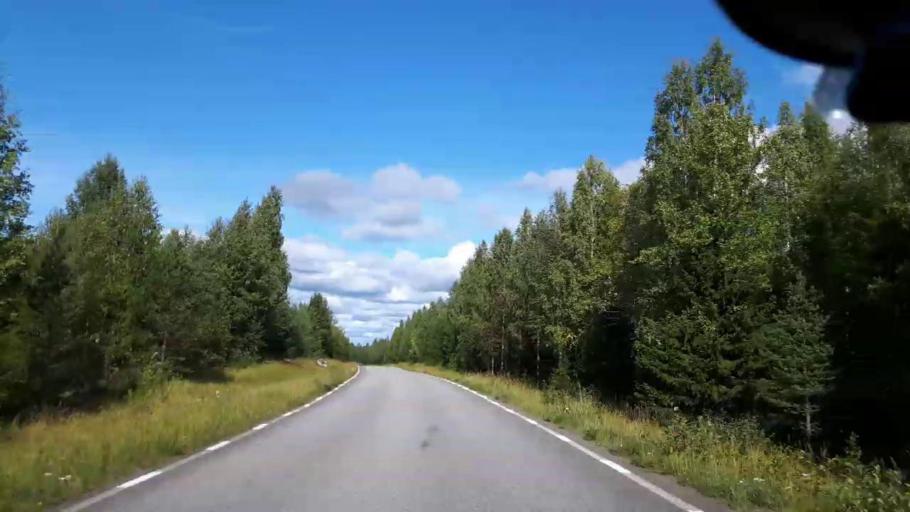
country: SE
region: Jaemtland
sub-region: OEstersunds Kommun
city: Brunflo
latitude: 63.2112
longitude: 15.2486
